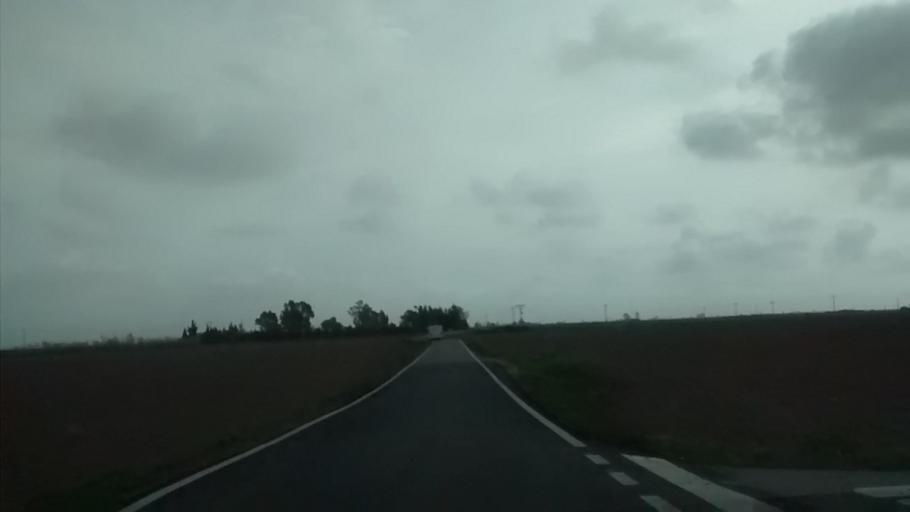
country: ES
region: Catalonia
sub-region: Provincia de Tarragona
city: Sant Carles de la Rapita
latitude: 40.6520
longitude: 0.6230
